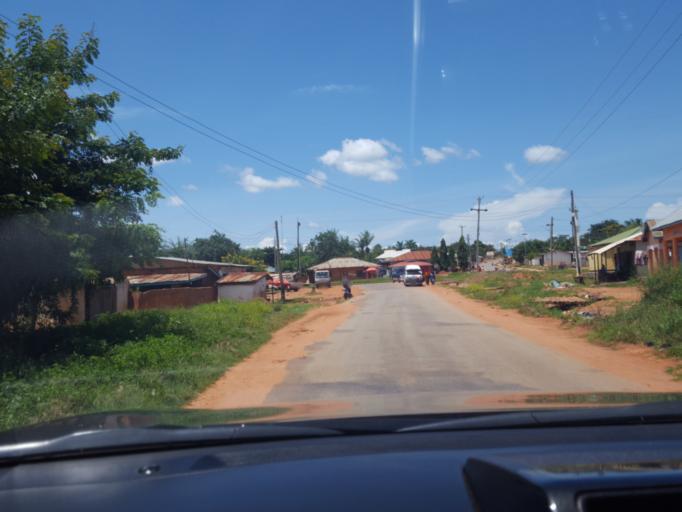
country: TZ
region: Kigoma
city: Kigoma
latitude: -4.8559
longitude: 29.6458
